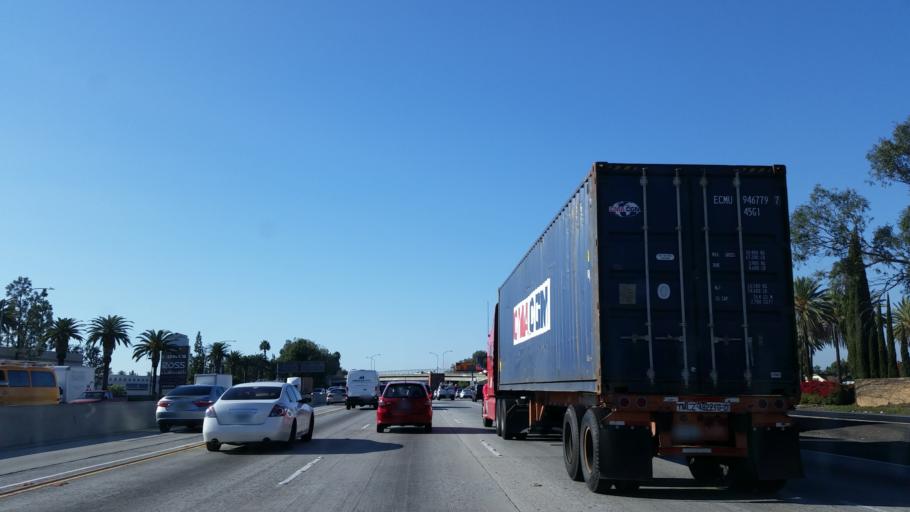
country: US
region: California
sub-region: Los Angeles County
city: Cerritos
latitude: 33.8714
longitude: -118.0574
